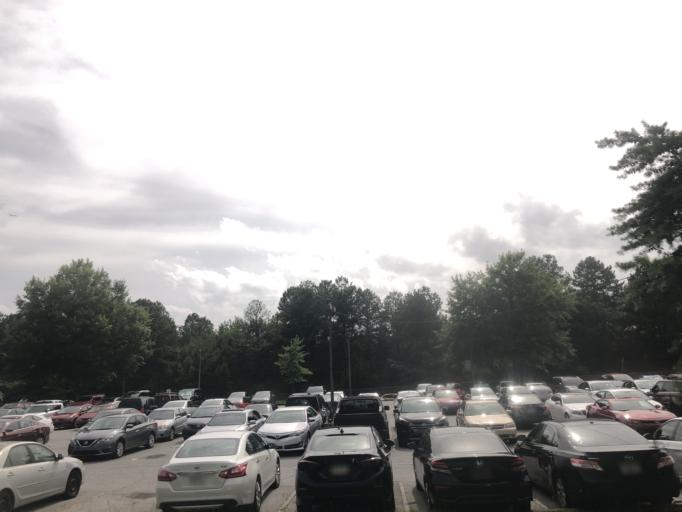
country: US
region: Georgia
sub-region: Fulton County
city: College Park
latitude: 33.6487
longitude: -84.4486
